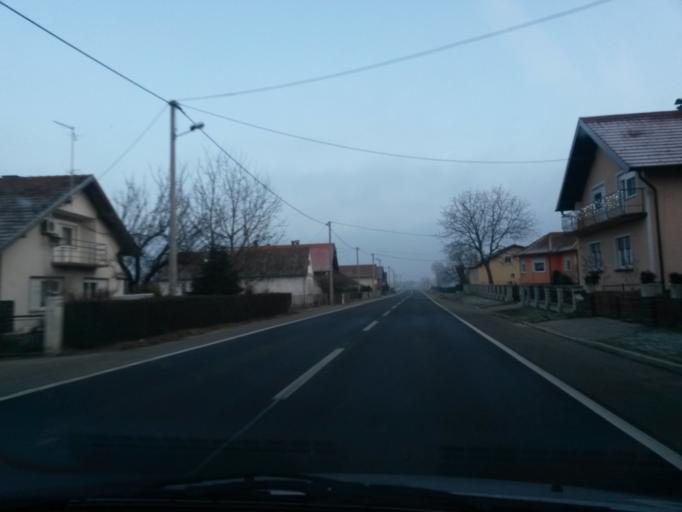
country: HR
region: Varazdinska
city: Ludbreg
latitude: 46.2176
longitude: 16.6855
